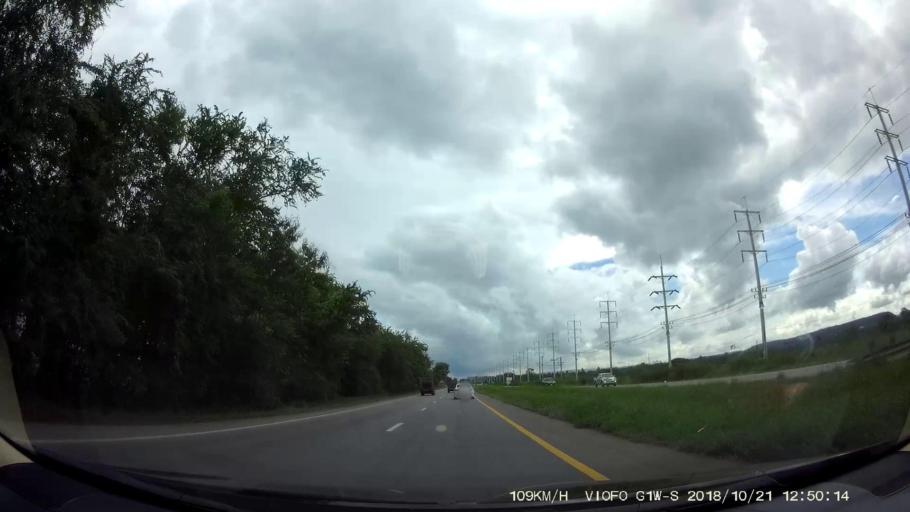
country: TH
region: Nakhon Ratchasima
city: Amphoe Sikhiu
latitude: 14.8851
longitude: 101.6889
